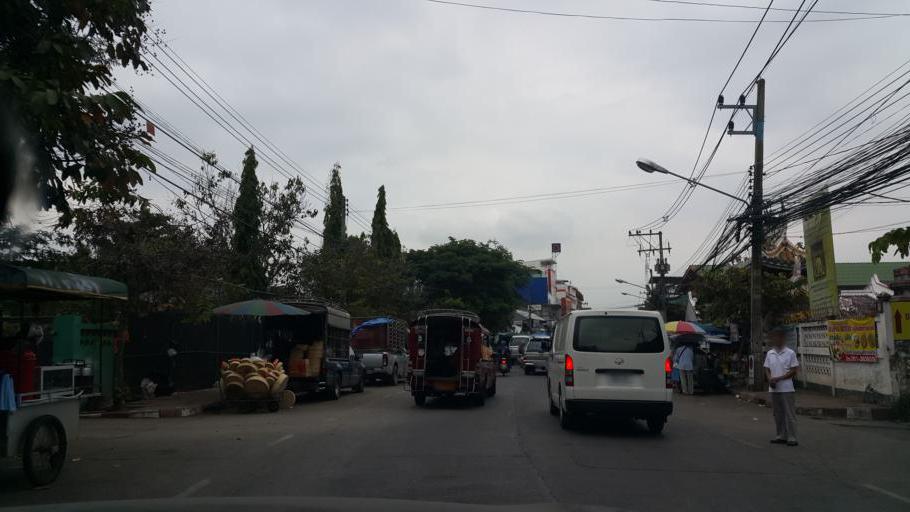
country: TH
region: Chiang Mai
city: Chiang Mai
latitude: 18.7959
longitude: 98.9965
